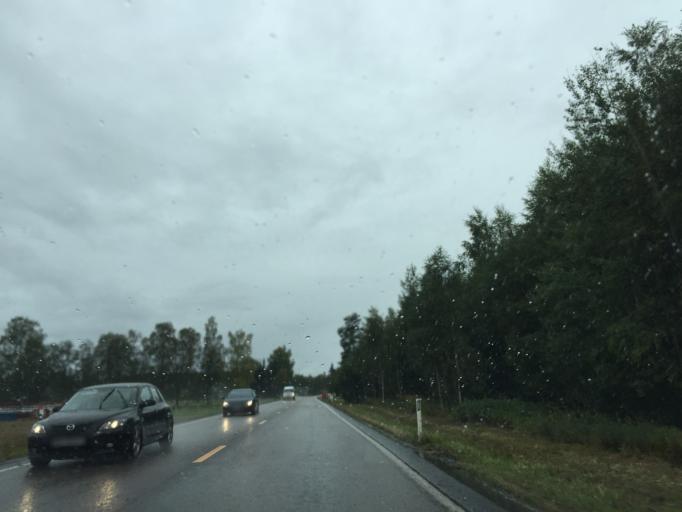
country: NO
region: Akershus
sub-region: Nes
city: Neskollen
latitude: 60.1395
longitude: 11.3876
